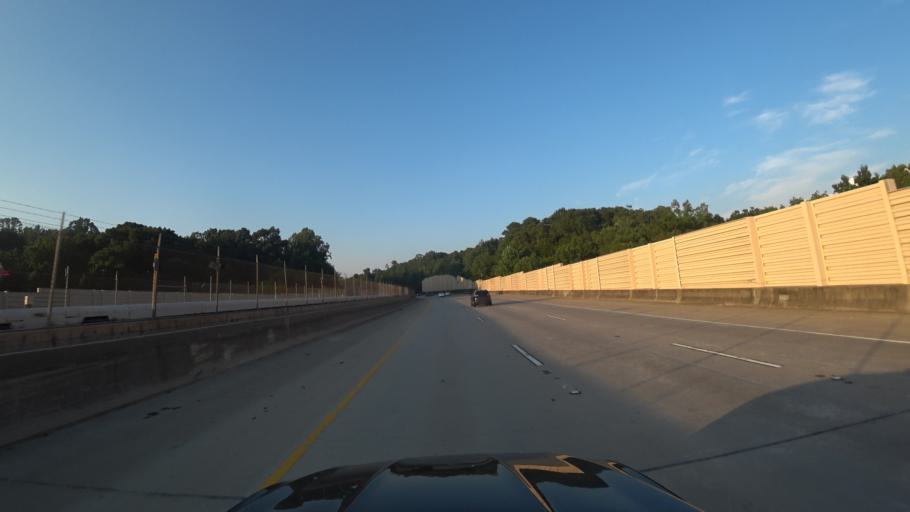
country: US
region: Georgia
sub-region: DeKalb County
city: North Atlanta
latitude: 33.8681
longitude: -84.3667
